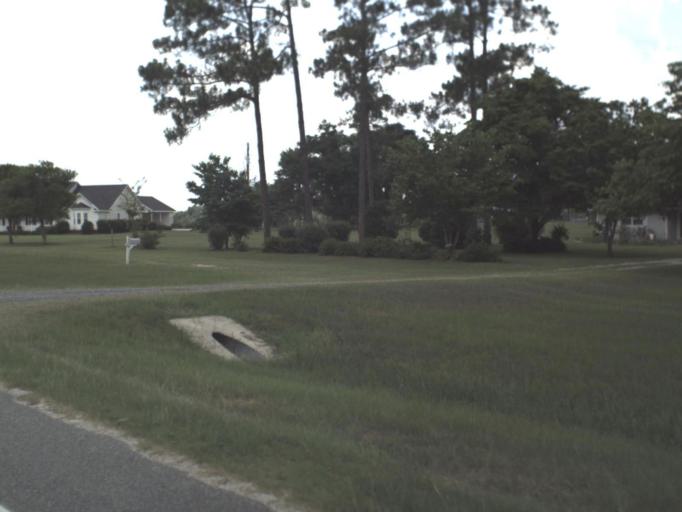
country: US
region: Florida
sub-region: Hamilton County
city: Jasper
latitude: 30.5240
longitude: -83.0114
